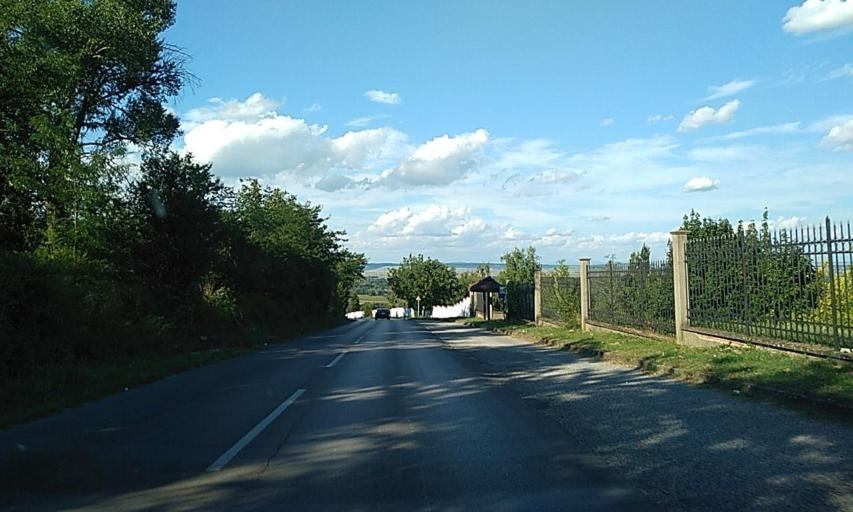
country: RS
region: Central Serbia
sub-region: Branicevski Okrug
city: Pozarevac
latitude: 44.6385
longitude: 21.2046
